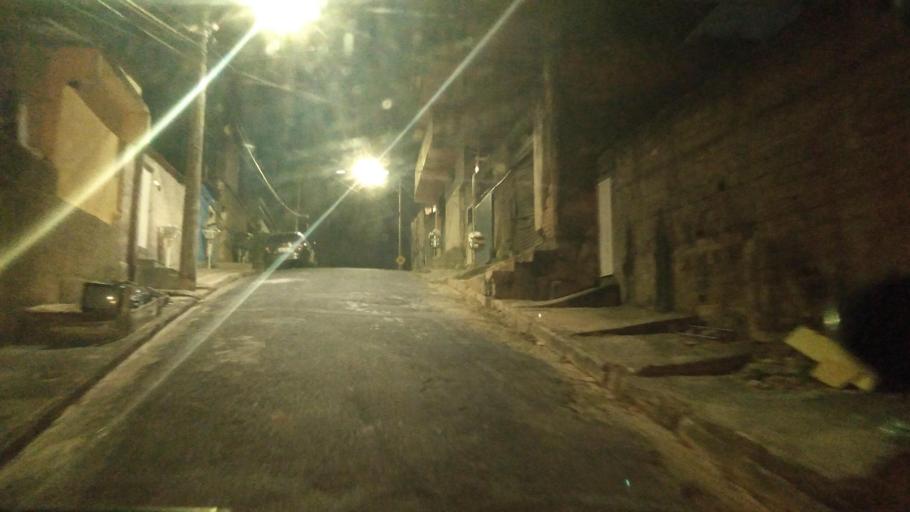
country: BR
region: Minas Gerais
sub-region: Belo Horizonte
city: Belo Horizonte
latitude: -19.8899
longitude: -43.9594
